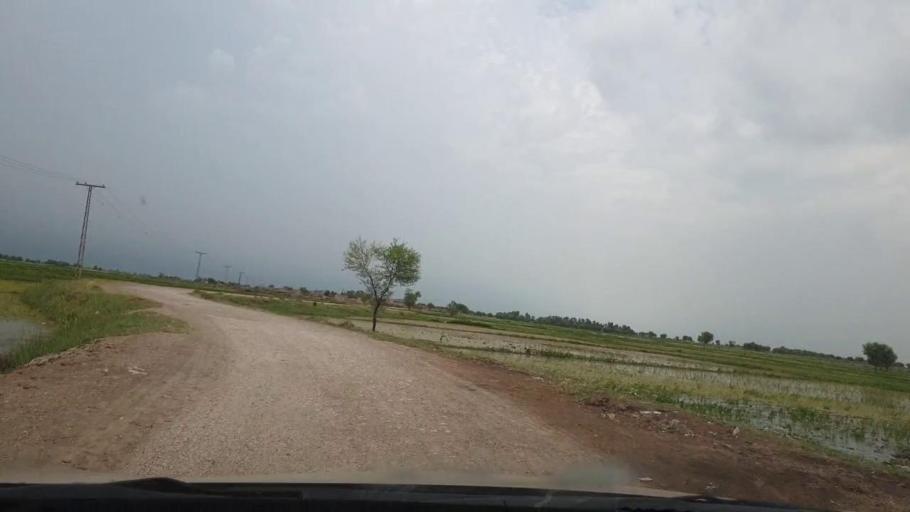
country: PK
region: Sindh
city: Ratodero
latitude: 27.8150
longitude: 68.3170
